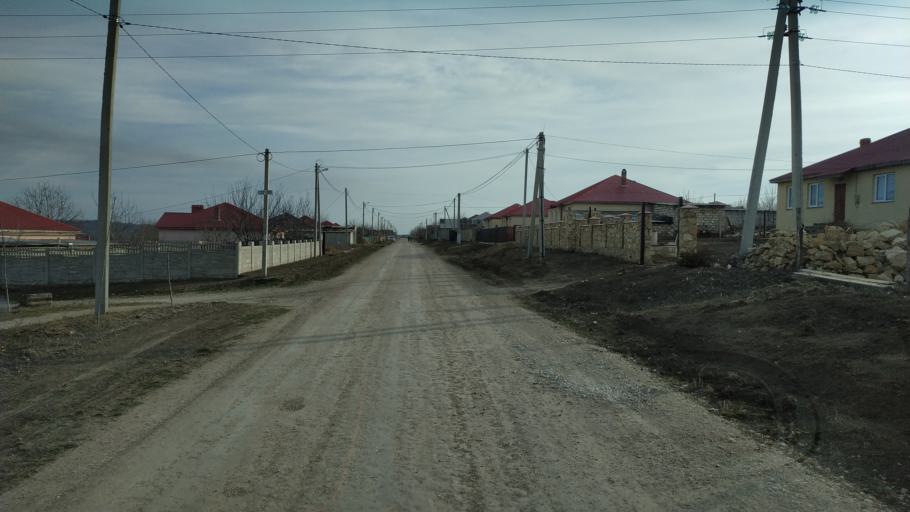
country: RO
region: Vaslui
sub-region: Comuna Dranceni
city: Dranceni
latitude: 46.8385
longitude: 28.1848
